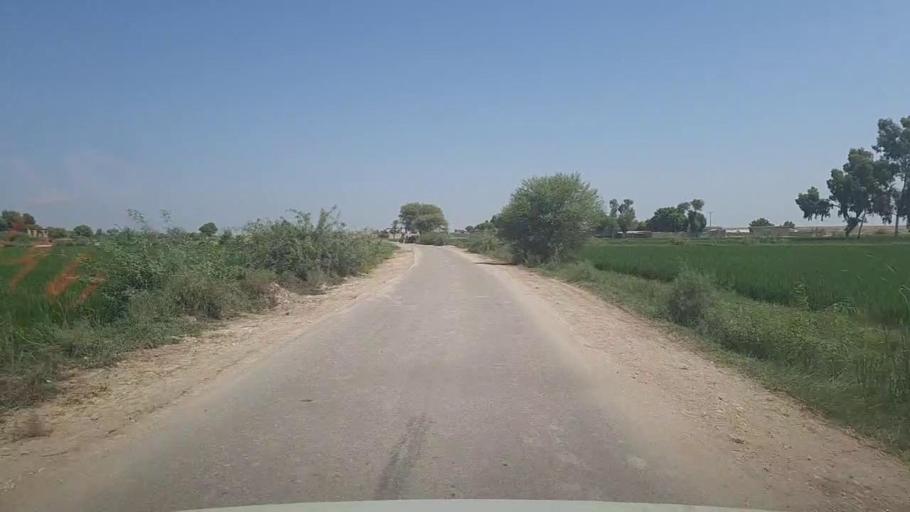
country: PK
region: Sindh
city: Kashmor
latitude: 28.2819
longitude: 69.4406
